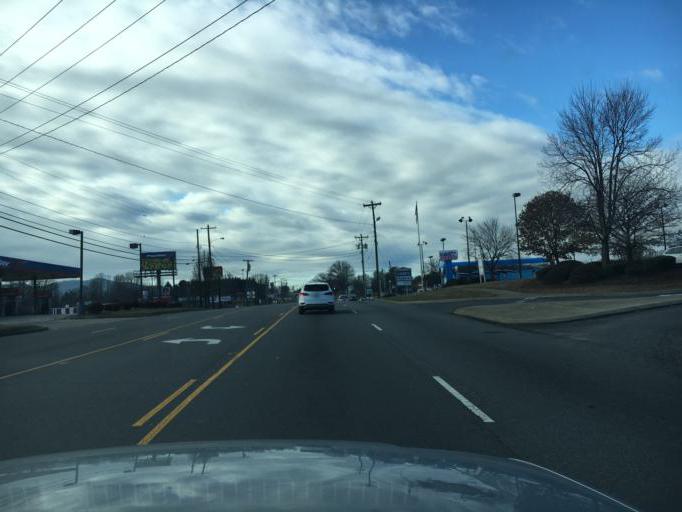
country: US
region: North Carolina
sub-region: Burke County
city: Salem
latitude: 35.7178
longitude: -81.6948
